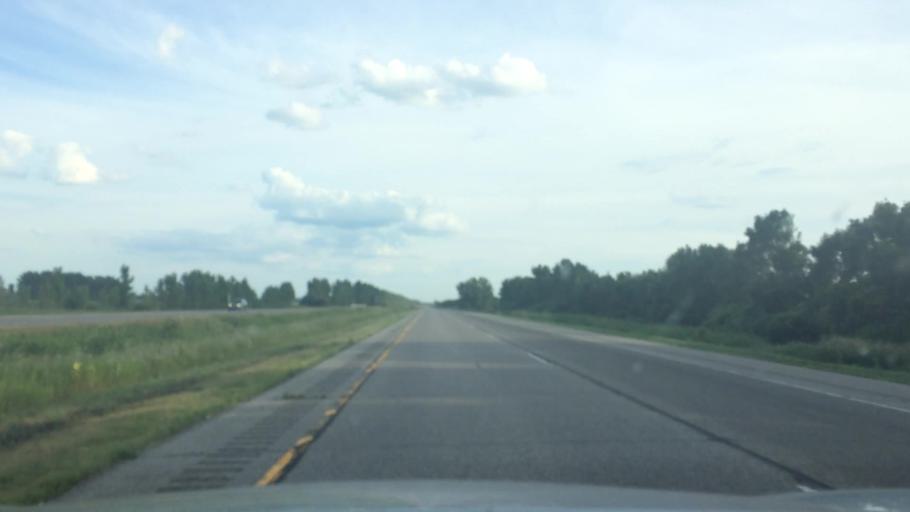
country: US
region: Wisconsin
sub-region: Portage County
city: Plover
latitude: 44.3630
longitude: -89.5207
